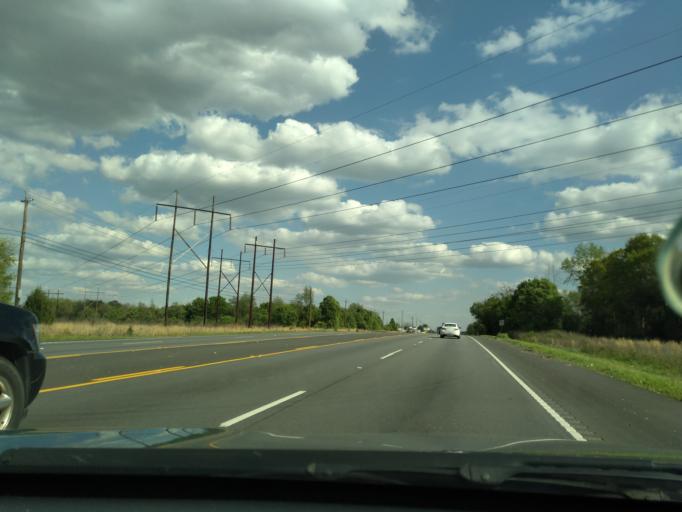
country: US
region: South Carolina
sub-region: Florence County
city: Florence
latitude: 34.2194
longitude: -79.7867
